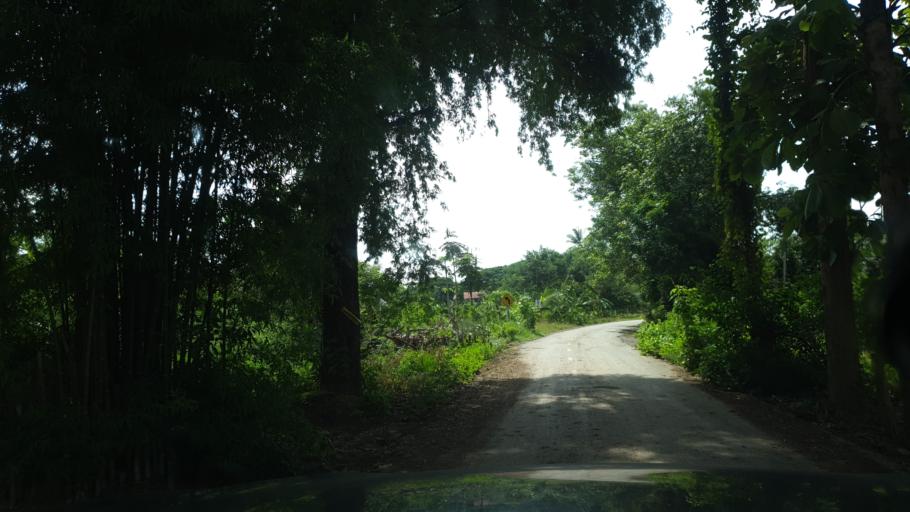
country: TH
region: Sukhothai
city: Sawankhalok
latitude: 17.2175
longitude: 99.7151
